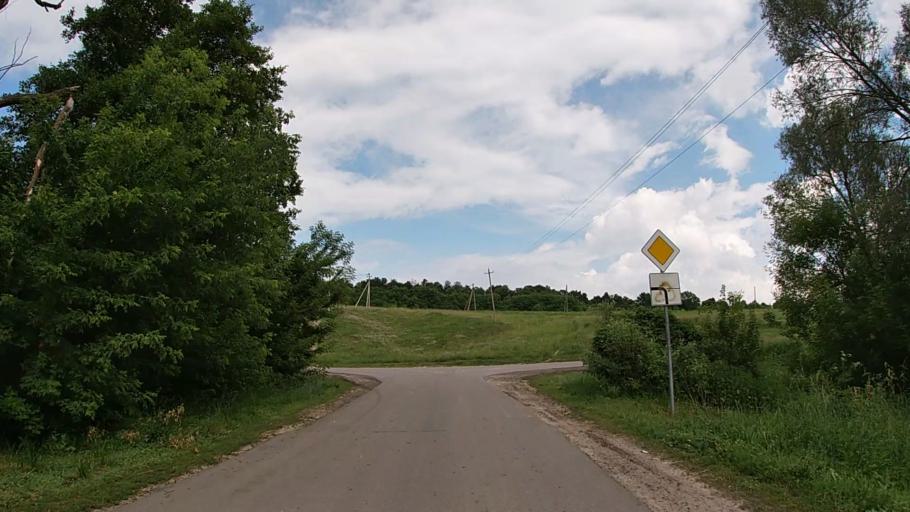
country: RU
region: Belgorod
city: Severnyy
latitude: 50.7267
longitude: 36.6112
